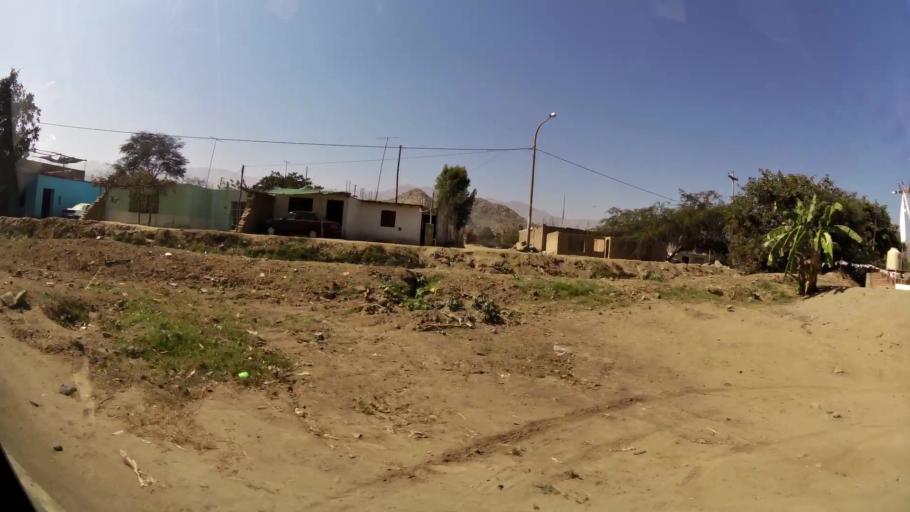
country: PE
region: Ica
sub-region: Provincia de Ica
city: San Juan Bautista
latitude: -13.9378
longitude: -75.6737
